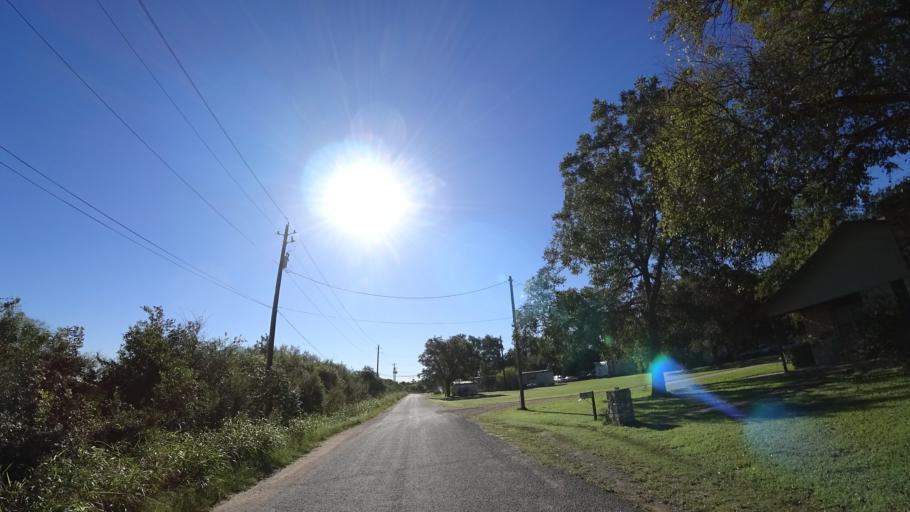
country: US
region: Texas
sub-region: Travis County
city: Hornsby Bend
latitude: 30.2380
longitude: -97.6548
